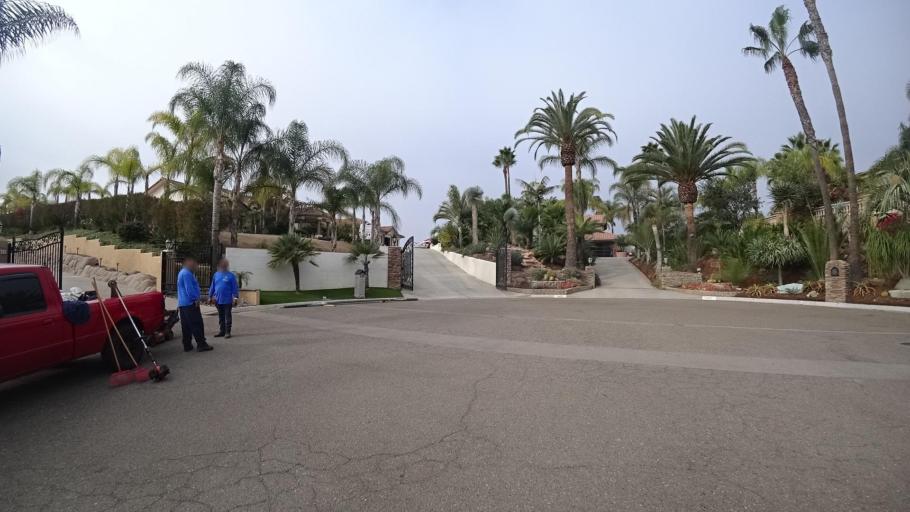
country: US
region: California
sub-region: San Diego County
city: Rancho San Diego
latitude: 32.7627
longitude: -116.9312
